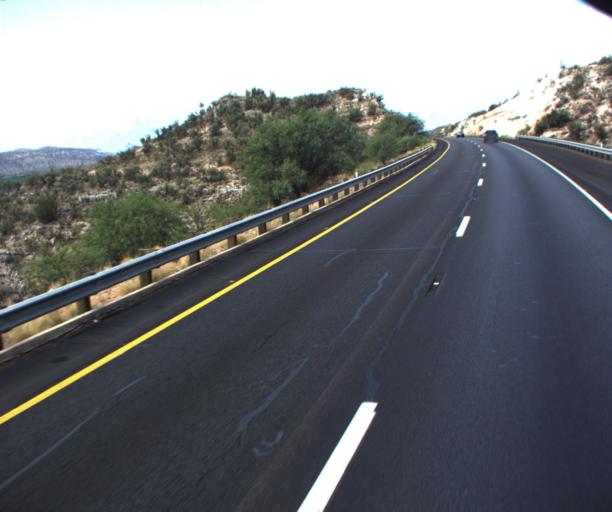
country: US
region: Arizona
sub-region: Yavapai County
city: Lake Montezuma
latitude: 34.6344
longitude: -111.8319
